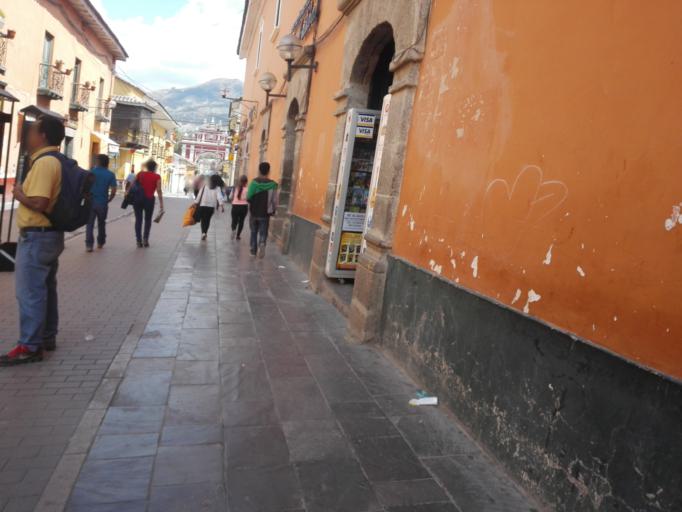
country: PE
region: Ayacucho
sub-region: Provincia de Huamanga
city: Ayacucho
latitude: -13.1616
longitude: -74.2267
